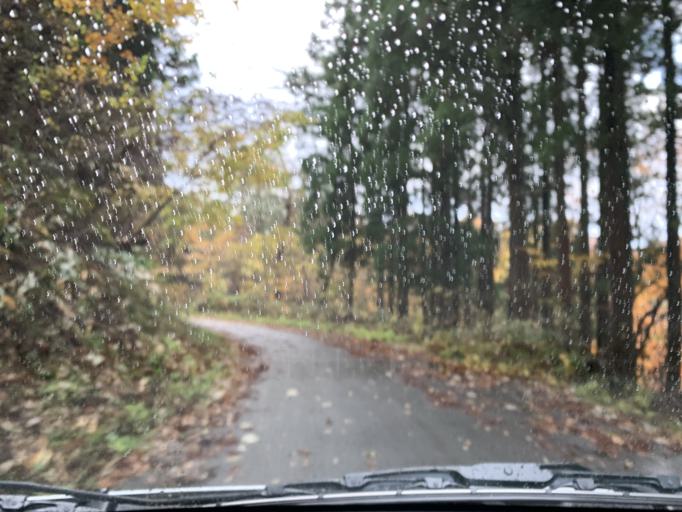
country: JP
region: Iwate
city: Mizusawa
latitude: 39.1030
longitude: 140.9562
